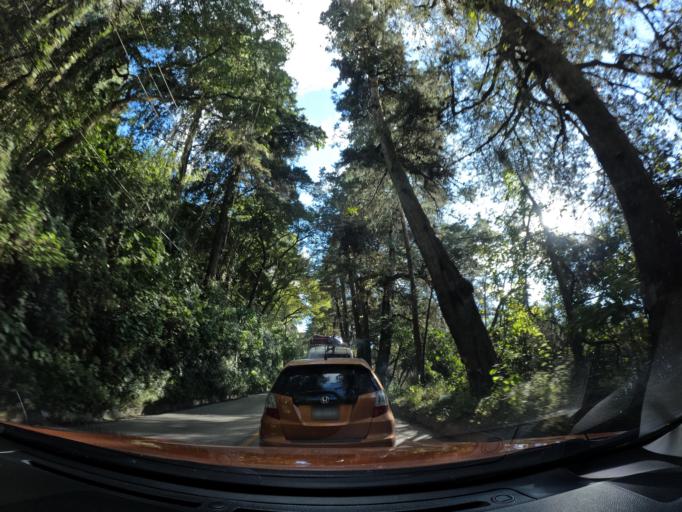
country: GT
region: Sacatepequez
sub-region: Municipio de Santa Maria de Jesus
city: Santa Maria de Jesus
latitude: 14.5053
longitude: -90.7145
